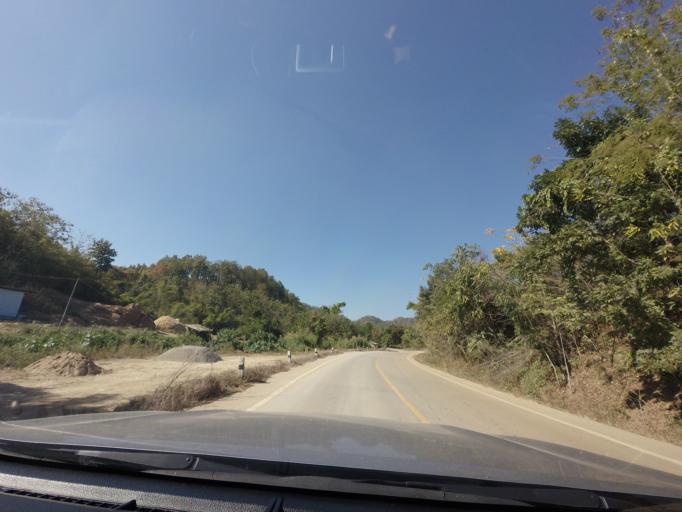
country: TH
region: Lampang
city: Chae Hom
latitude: 18.5363
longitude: 99.6422
